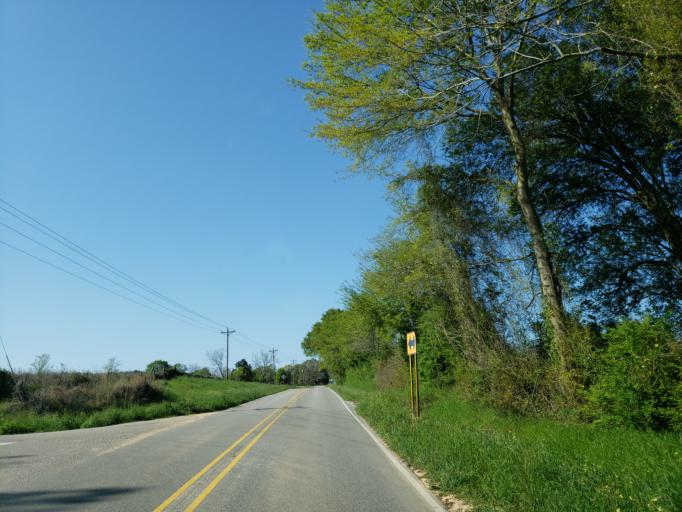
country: US
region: Mississippi
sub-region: Jones County
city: Ellisville
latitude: 31.5833
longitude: -89.3784
